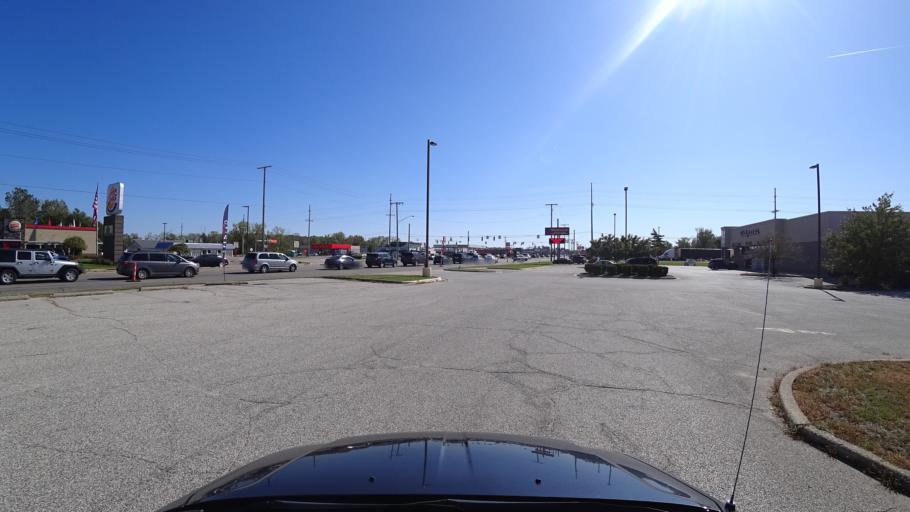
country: US
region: Indiana
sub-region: LaPorte County
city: Michigan City
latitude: 41.6815
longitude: -86.8944
